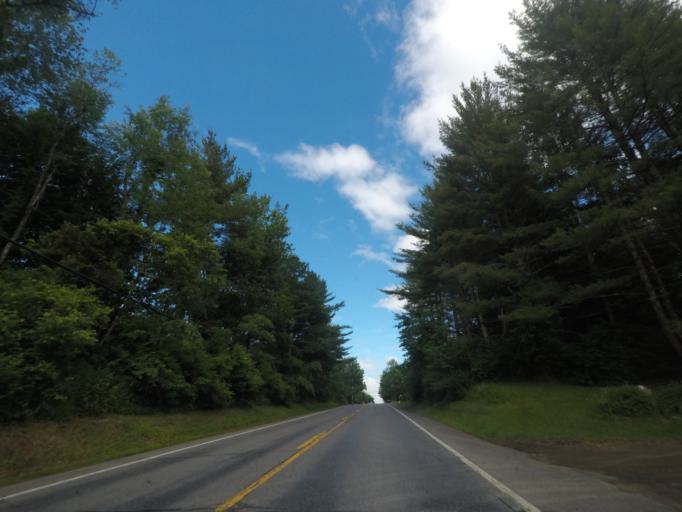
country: US
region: New York
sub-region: Columbia County
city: Philmont
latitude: 42.2088
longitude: -73.6558
